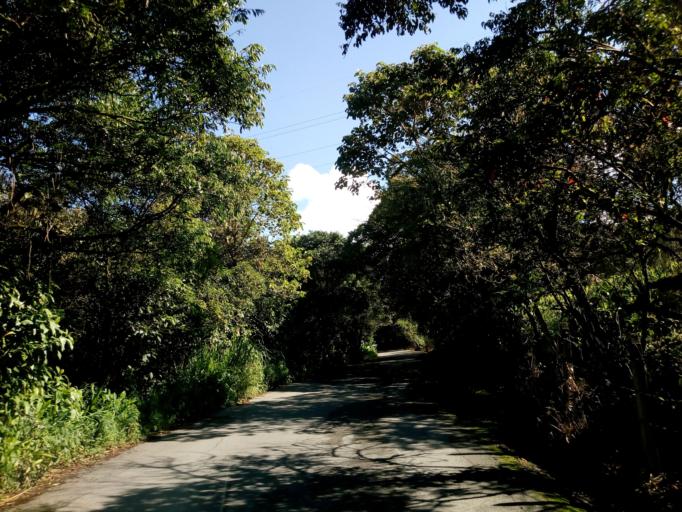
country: CO
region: Boyaca
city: Moniquira
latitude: 5.8658
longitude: -73.5535
